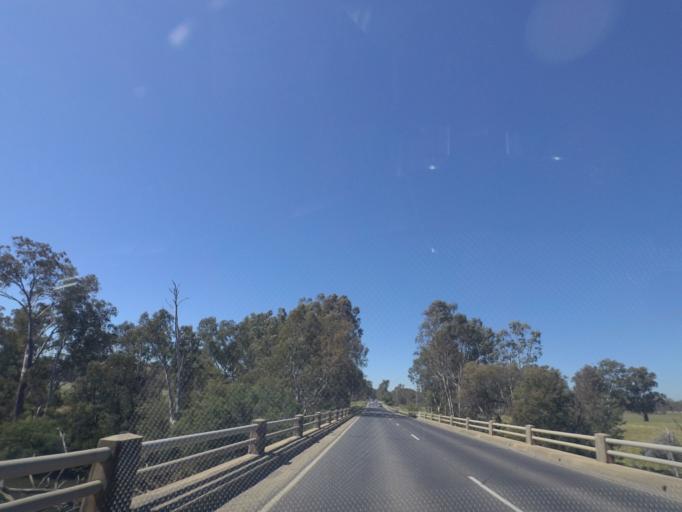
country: AU
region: Victoria
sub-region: Murrindindi
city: Kinglake West
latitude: -37.0277
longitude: 145.1079
